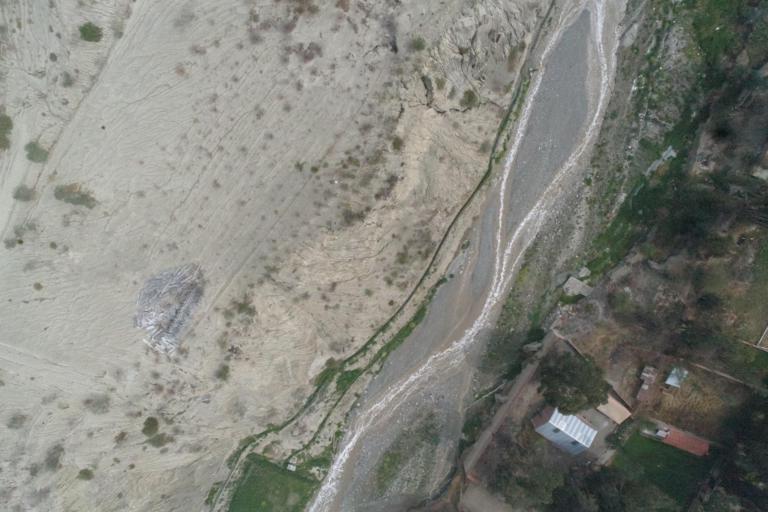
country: BO
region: La Paz
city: La Paz
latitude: -16.6025
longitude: -68.0668
